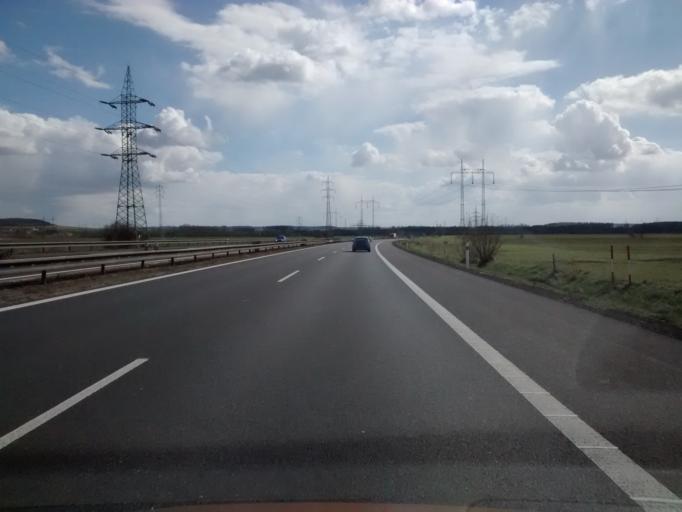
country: CZ
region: Central Bohemia
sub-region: Okres Melnik
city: Veltrusy
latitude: 50.2884
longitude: 14.3507
